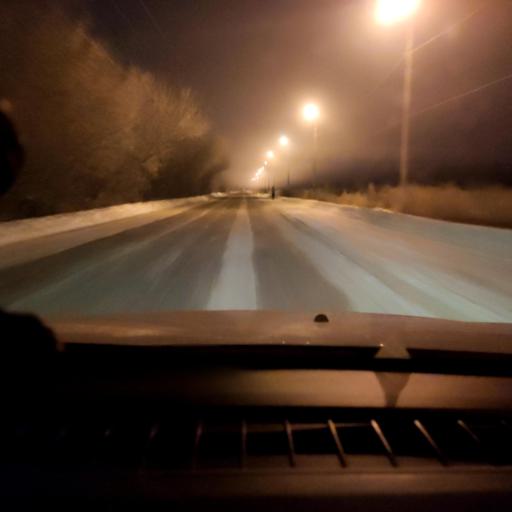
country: RU
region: Samara
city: Samara
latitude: 53.1458
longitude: 50.1415
